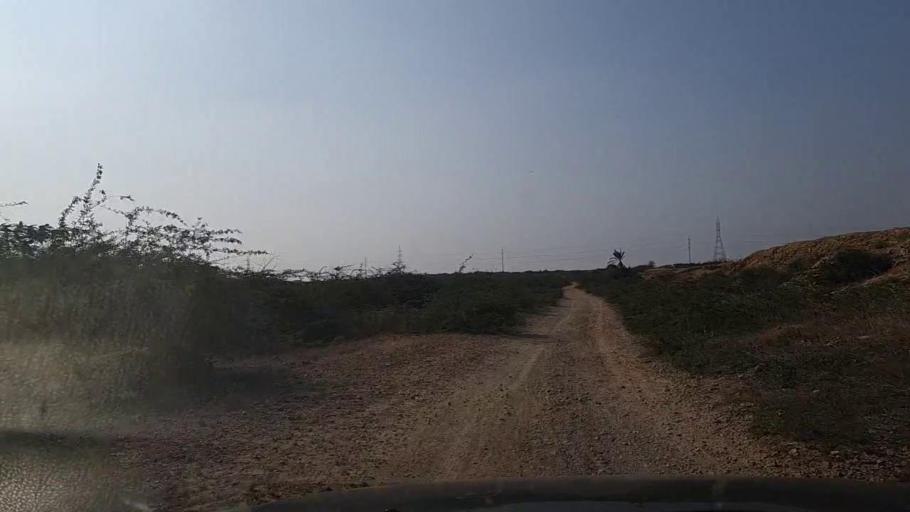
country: PK
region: Sindh
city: Gharo
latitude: 24.7520
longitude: 67.5466
